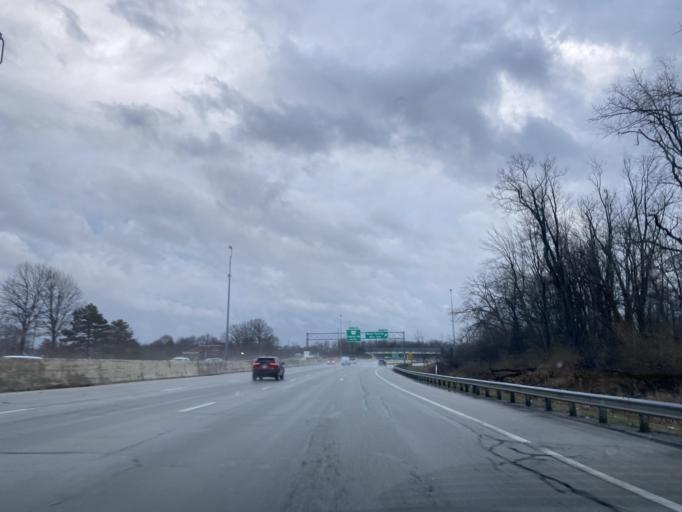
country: IN
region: Maharashtra
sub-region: Pune Division
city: Baramati
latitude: 18.1724
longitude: 74.4012
